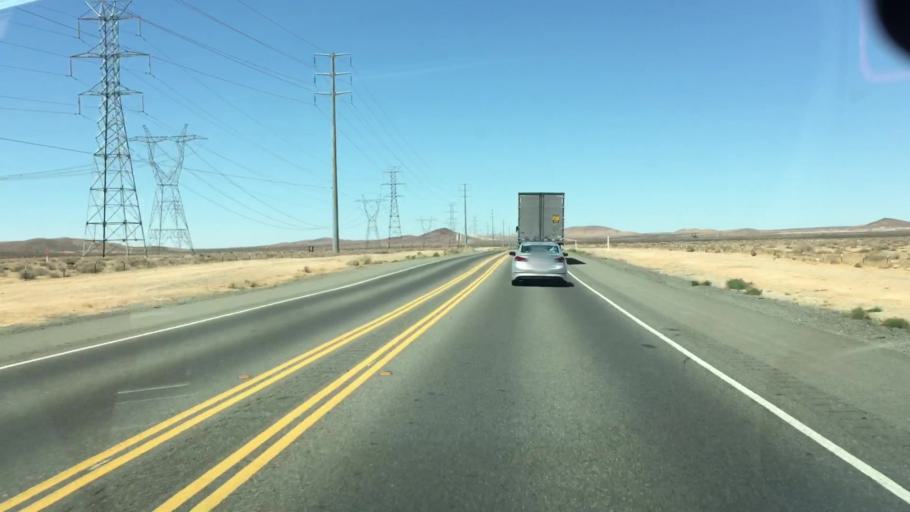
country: US
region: California
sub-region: Kern County
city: Boron
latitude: 34.8231
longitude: -117.4947
